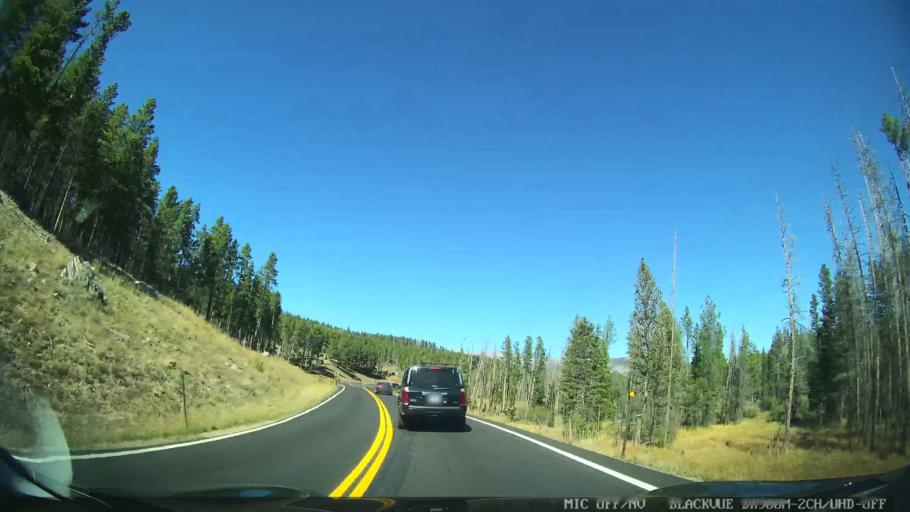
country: US
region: Colorado
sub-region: Larimer County
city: Estes Park
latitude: 40.3286
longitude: -105.5993
